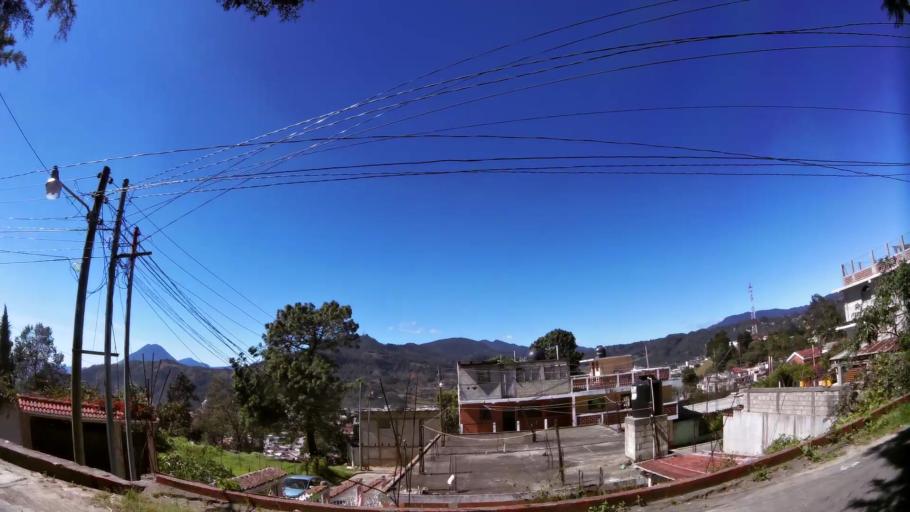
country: GT
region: Solola
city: Solola
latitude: 14.7737
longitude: -91.1805
